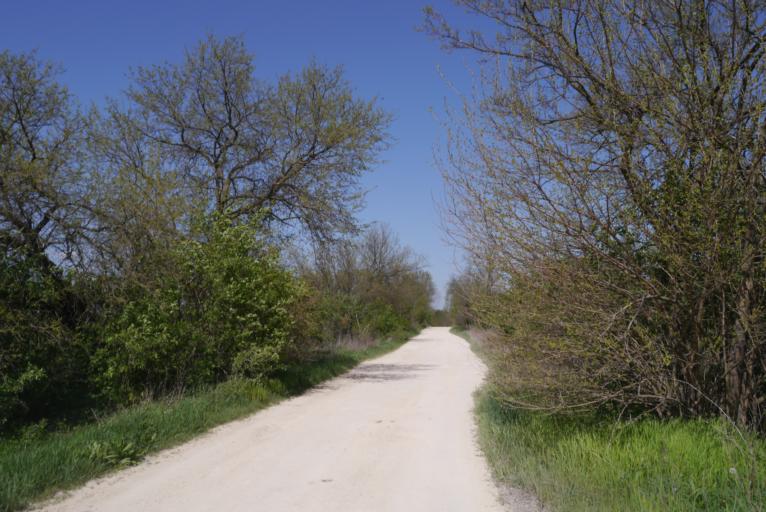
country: HU
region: Komarom-Esztergom
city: Kesztolc
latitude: 47.6960
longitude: 18.7974
